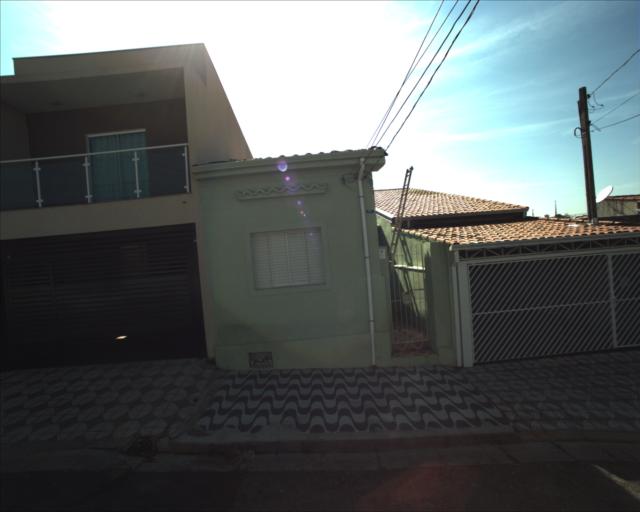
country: BR
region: Sao Paulo
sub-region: Sorocaba
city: Sorocaba
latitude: -23.4872
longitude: -47.4605
